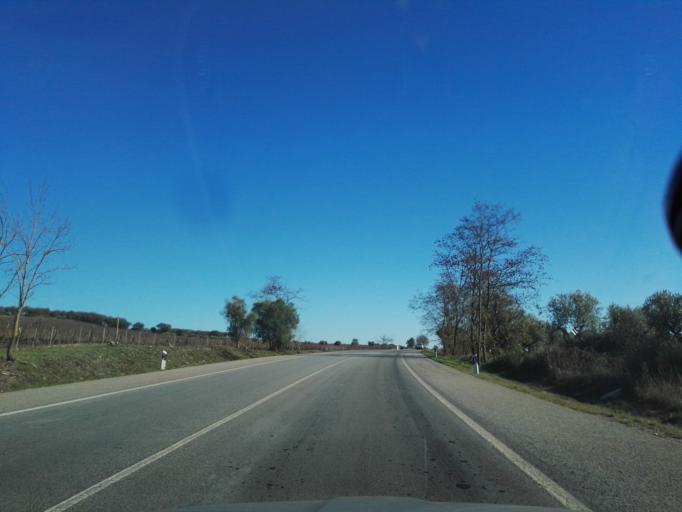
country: PT
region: Evora
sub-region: Estremoz
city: Estremoz
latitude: 38.8323
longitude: -7.5414
